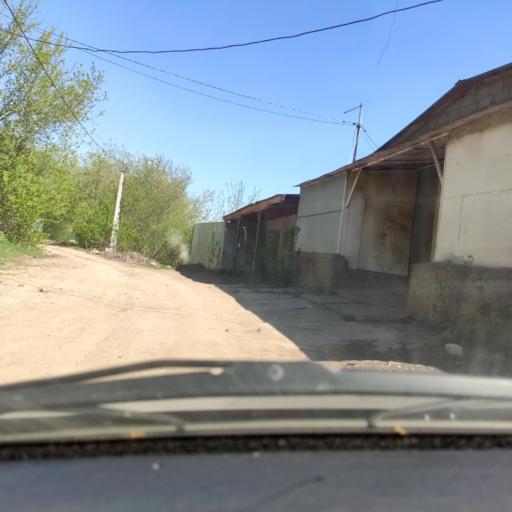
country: RU
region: Bashkortostan
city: Ufa
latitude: 54.8103
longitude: 56.1472
